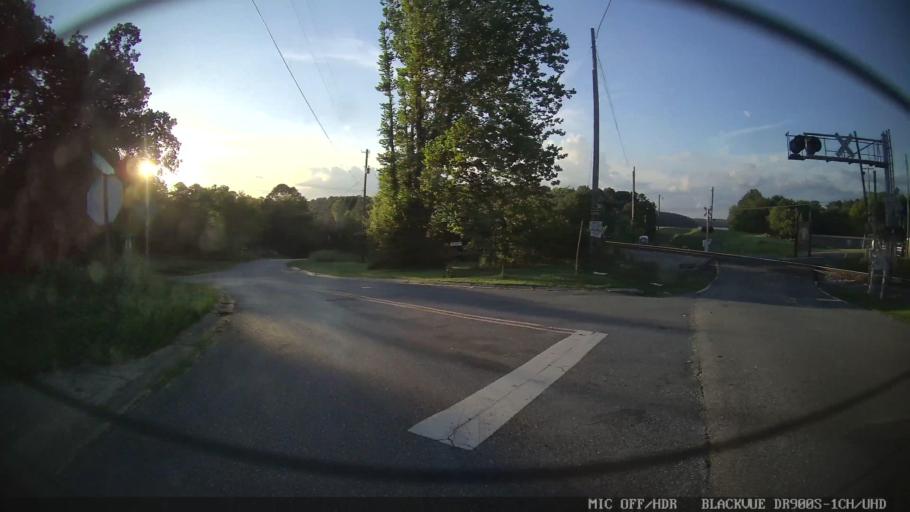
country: US
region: Georgia
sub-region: Bartow County
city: Emerson
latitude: 34.1085
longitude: -84.7123
